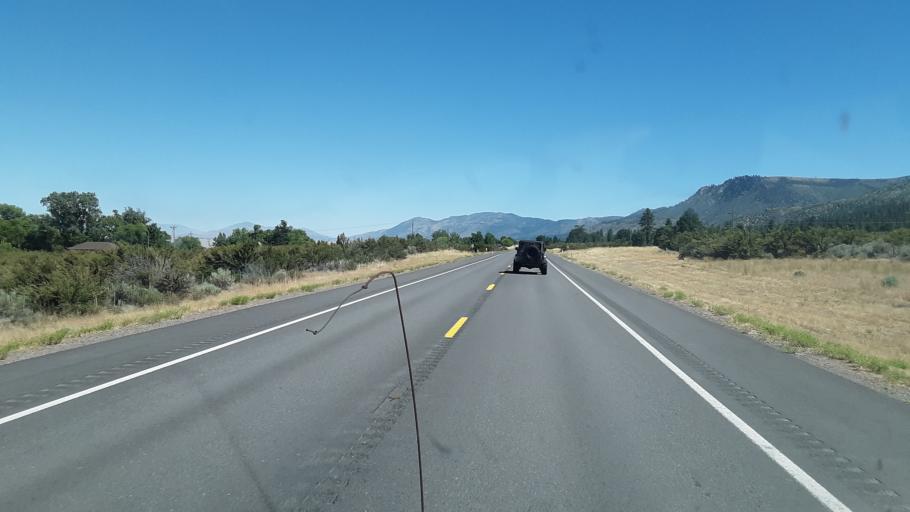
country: US
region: California
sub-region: Lassen County
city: Janesville
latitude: 40.2719
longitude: -120.4800
